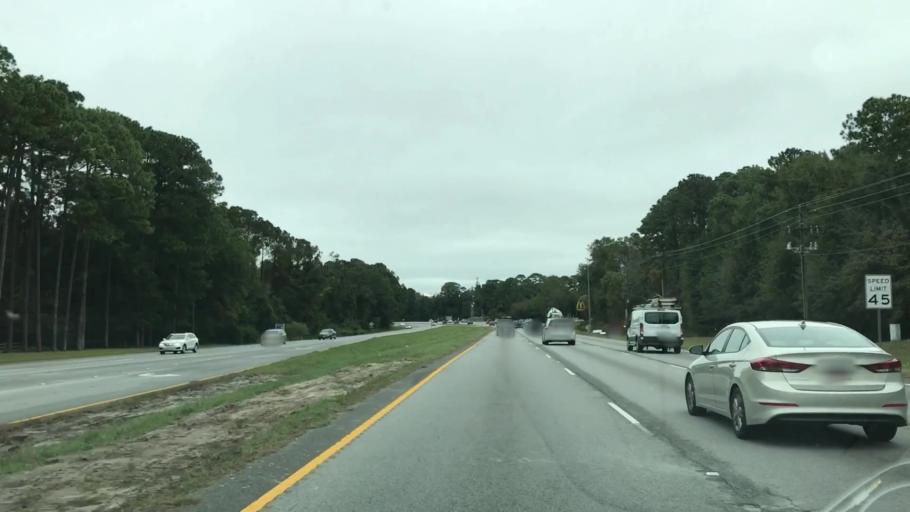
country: US
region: South Carolina
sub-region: Beaufort County
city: Bluffton
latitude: 32.2436
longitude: -80.8259
